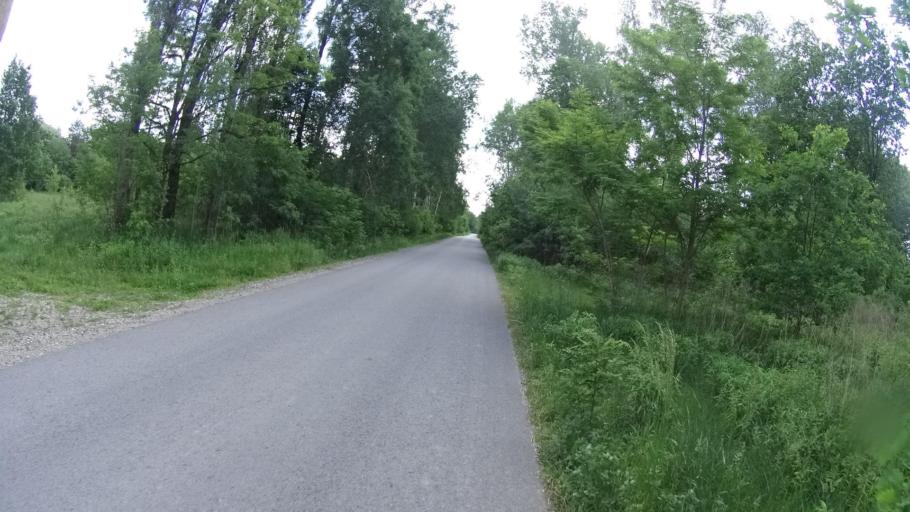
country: PL
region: Masovian Voivodeship
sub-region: Powiat pruszkowski
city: Nadarzyn
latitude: 52.0741
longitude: 20.8184
